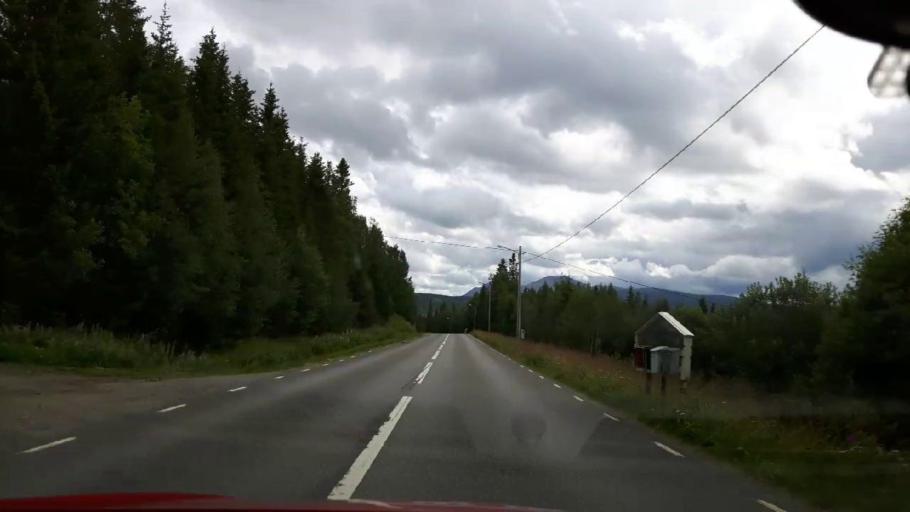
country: NO
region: Nord-Trondelag
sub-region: Lierne
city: Sandvika
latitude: 64.3925
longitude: 14.3703
